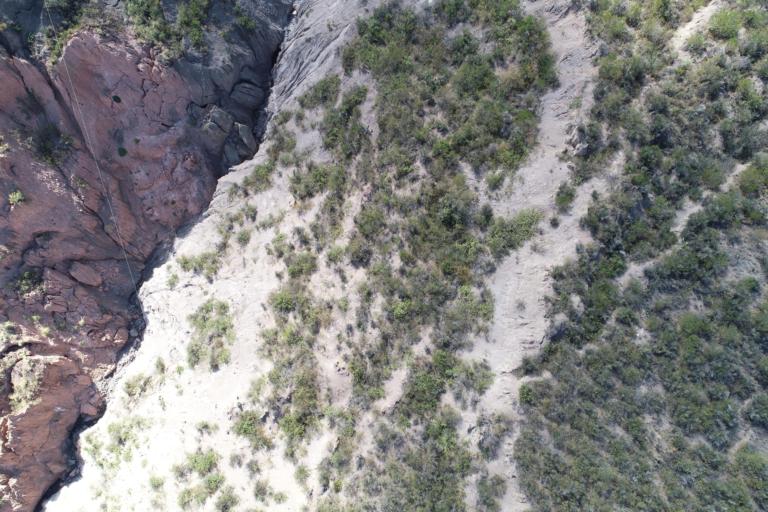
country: BO
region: La Paz
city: La Paz
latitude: -16.6206
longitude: -68.0384
